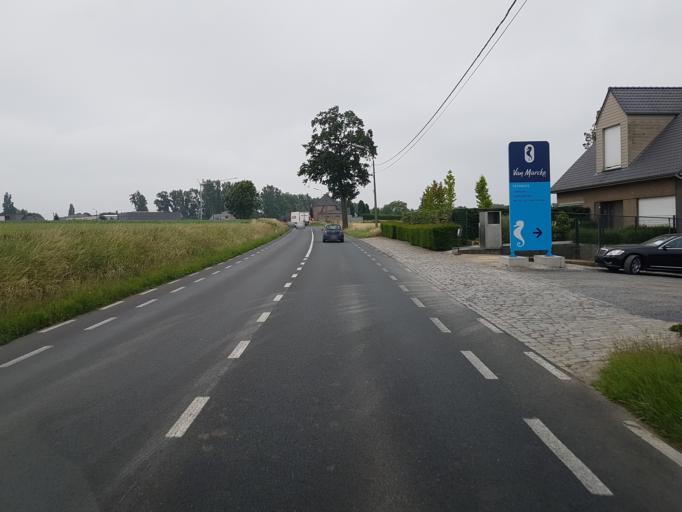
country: BE
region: Flanders
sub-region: Provincie Oost-Vlaanderen
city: Perre
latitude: 50.8550
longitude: 3.8569
